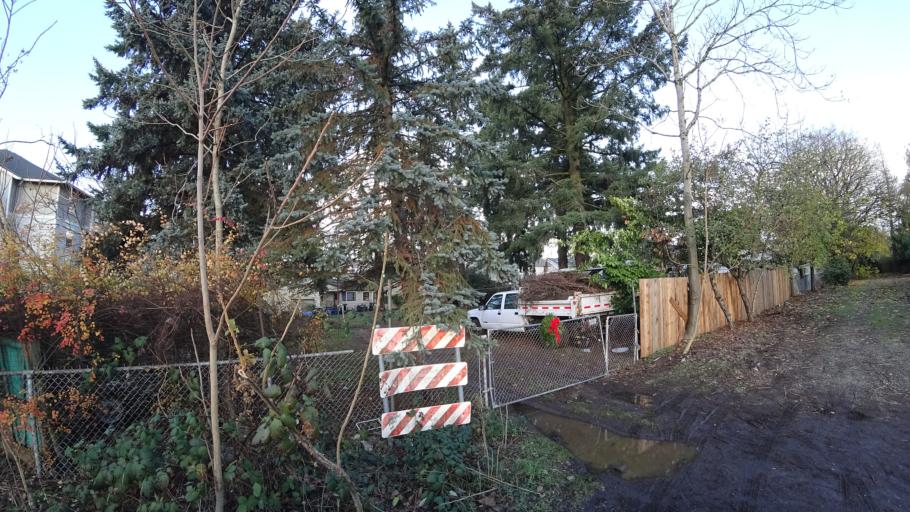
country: US
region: Oregon
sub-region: Multnomah County
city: Lents
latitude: 45.5219
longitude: -122.5539
